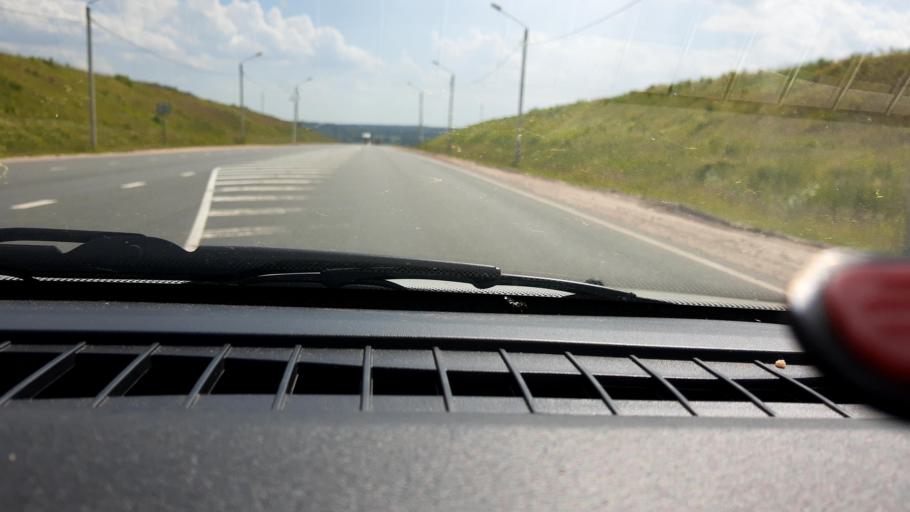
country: RU
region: Nizjnij Novgorod
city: Kstovo
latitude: 56.0878
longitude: 44.1344
